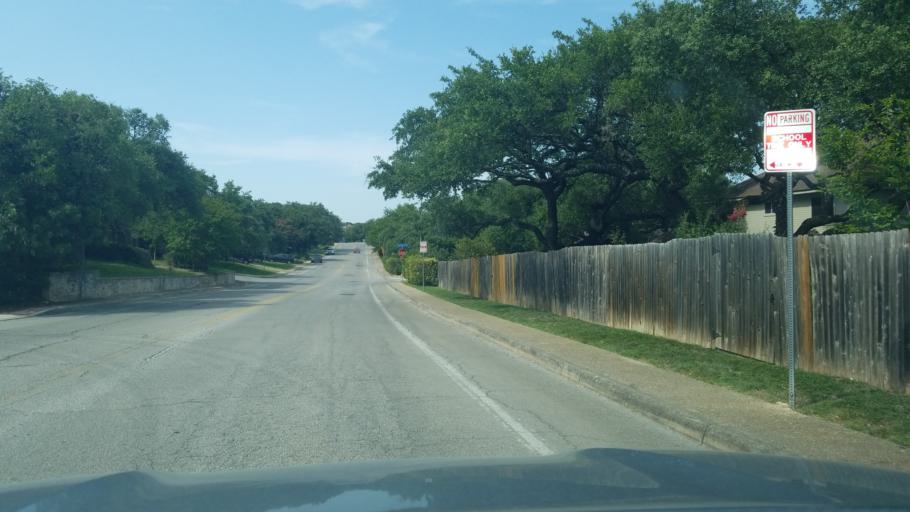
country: US
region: Texas
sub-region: Bexar County
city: Hollywood Park
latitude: 29.6265
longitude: -98.4883
